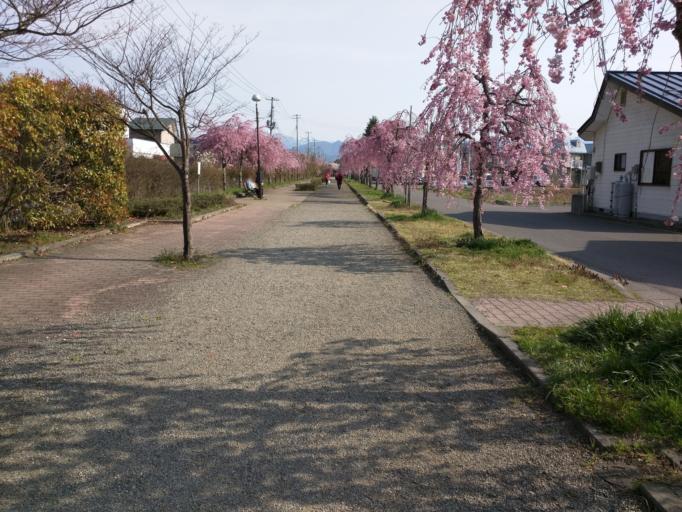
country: JP
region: Fukushima
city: Kitakata
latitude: 37.6527
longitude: 139.8650
